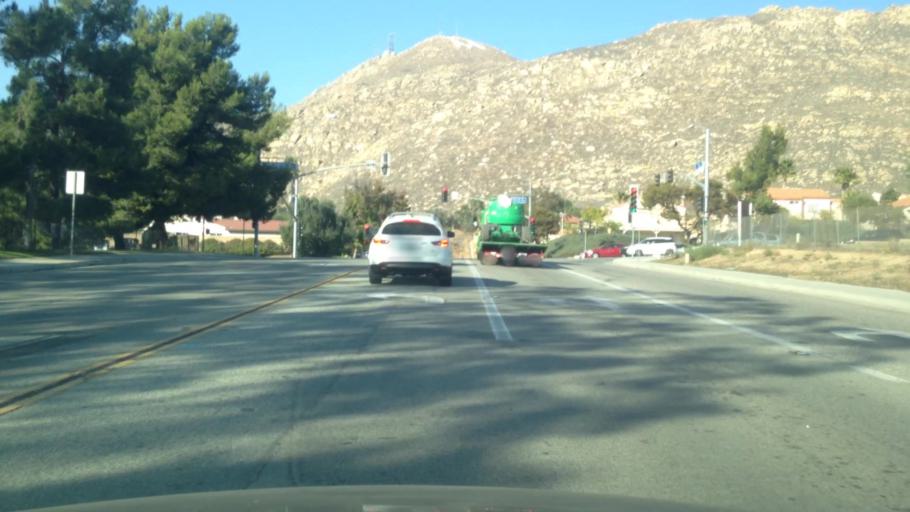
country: US
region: California
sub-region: Riverside County
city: Moreno Valley
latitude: 33.9458
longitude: -117.2790
